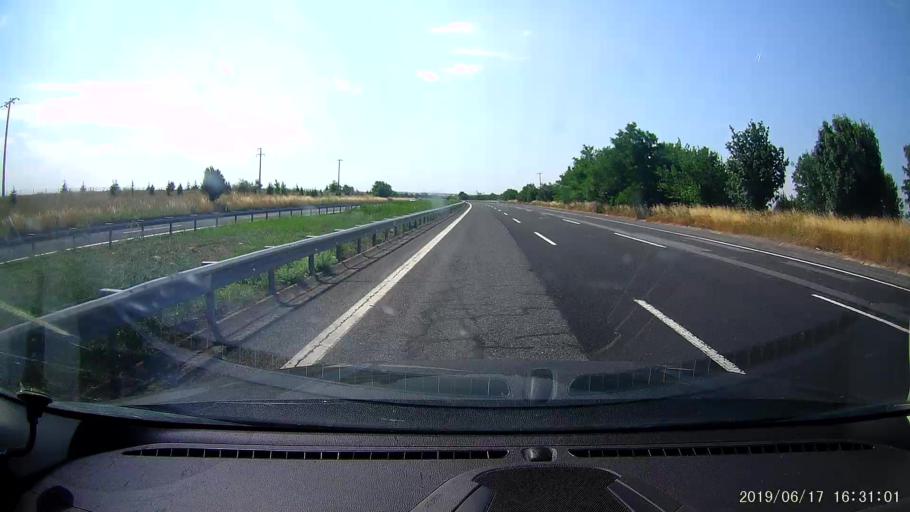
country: TR
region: Tekirdag
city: Beyazkoy
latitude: 41.3567
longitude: 27.6405
